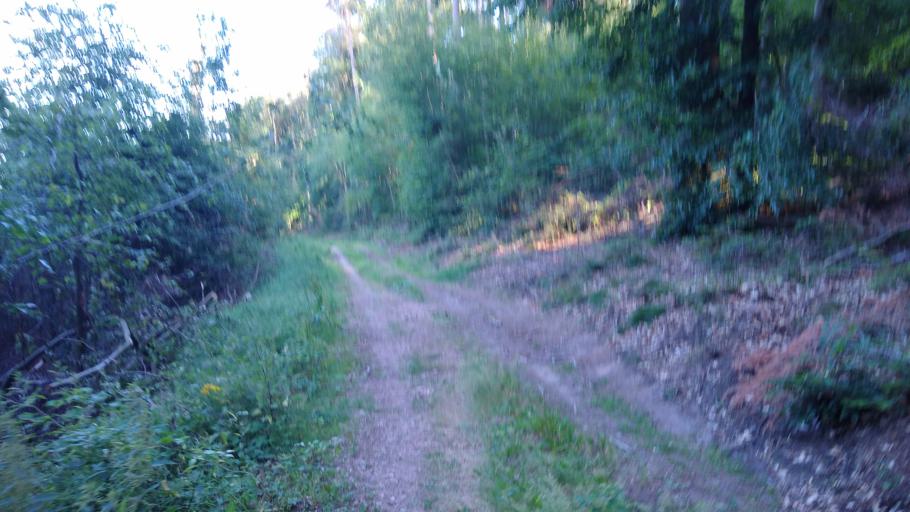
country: DE
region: Hesse
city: Reichelsheim
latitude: 49.6766
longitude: 8.8991
